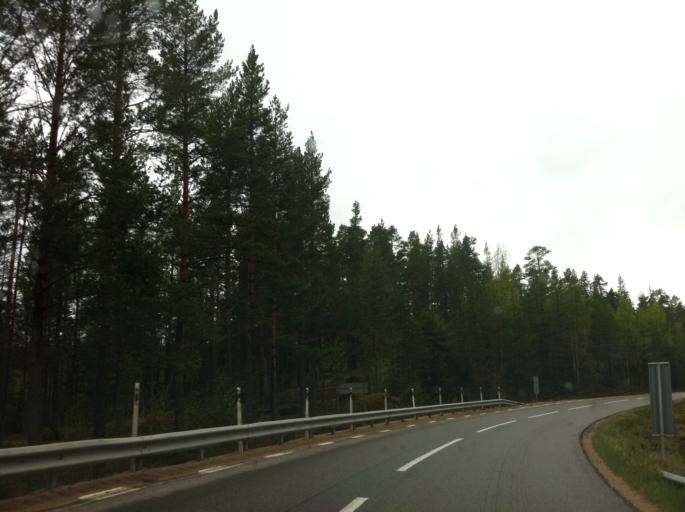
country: SE
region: Jaemtland
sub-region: Harjedalens Kommun
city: Sveg
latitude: 62.0298
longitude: 14.4089
